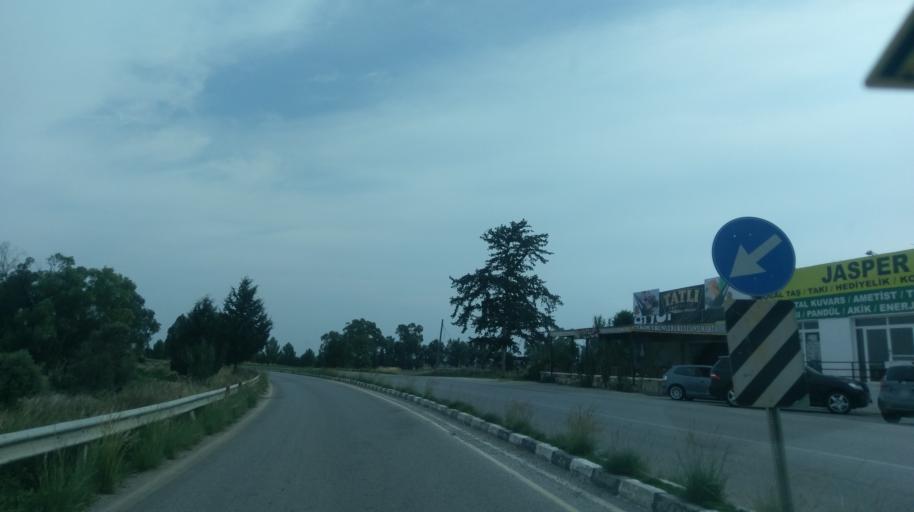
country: CY
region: Ammochostos
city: Trikomo
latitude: 35.2762
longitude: 33.8524
